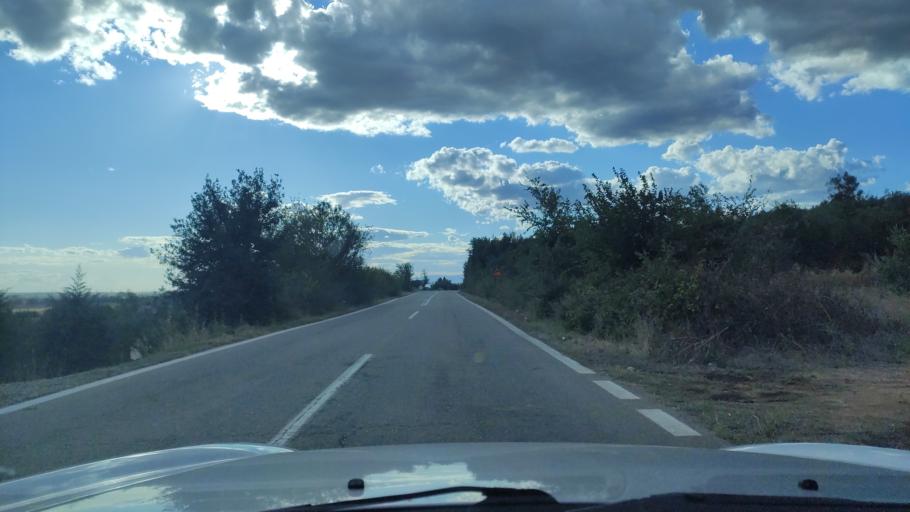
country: GR
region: East Macedonia and Thrace
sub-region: Nomos Rodopis
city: Iasmos
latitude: 41.1187
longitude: 25.1101
